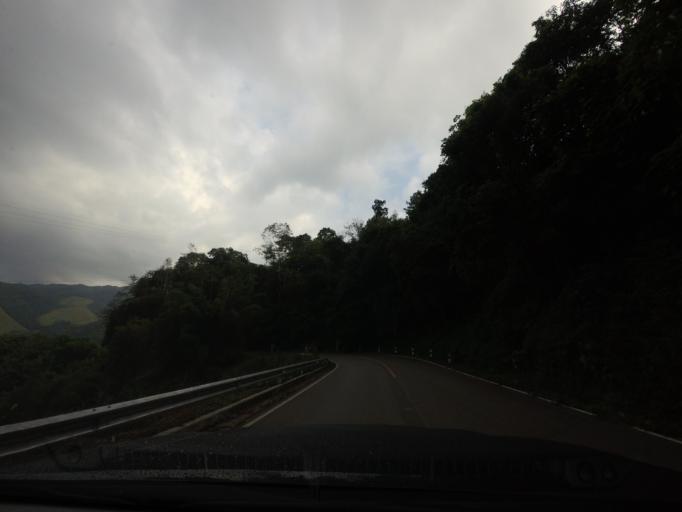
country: TH
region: Nan
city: Bo Kluea
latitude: 19.2752
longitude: 101.1763
